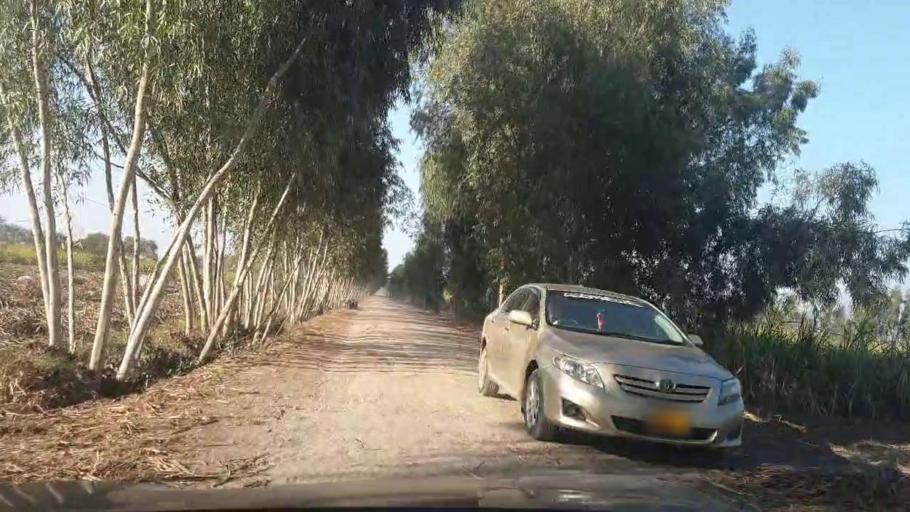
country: PK
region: Sindh
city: Ubauro
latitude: 28.1452
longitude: 69.6105
